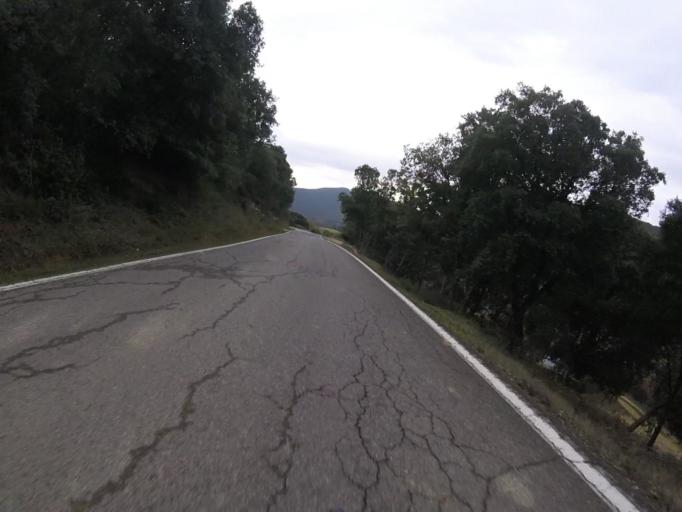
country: ES
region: Navarre
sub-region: Provincia de Navarra
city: Estella
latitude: 42.7100
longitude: -2.0491
